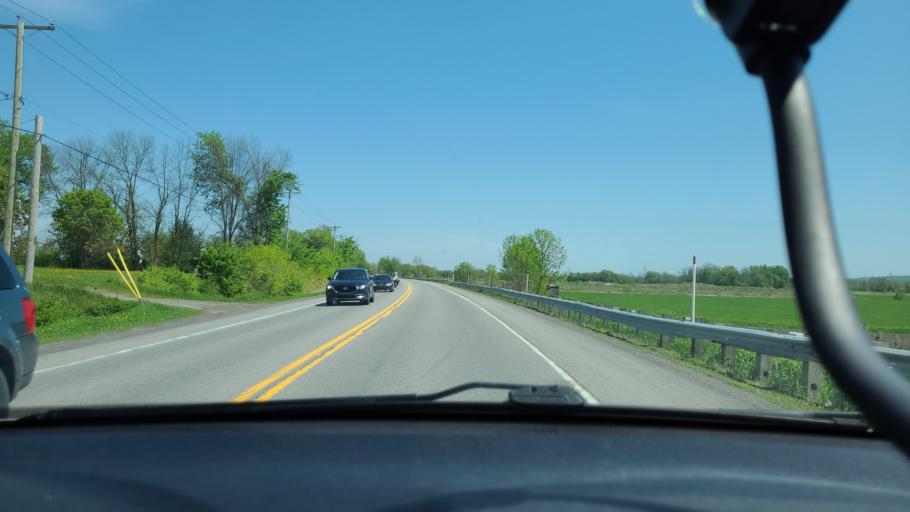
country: CA
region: Quebec
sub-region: Laurentides
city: Mirabel
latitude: 45.6104
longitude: -74.0774
